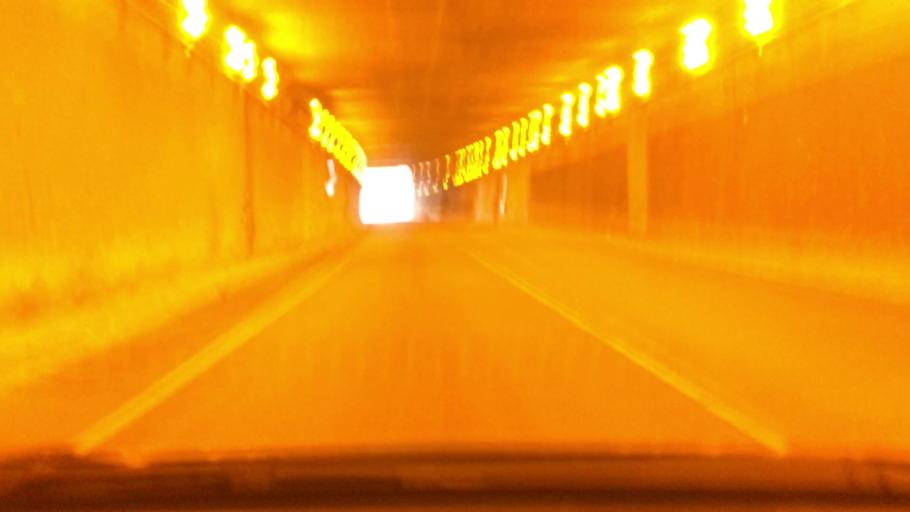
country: JP
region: Hiroshima
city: Ono-hara
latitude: 34.2573
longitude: 132.2243
